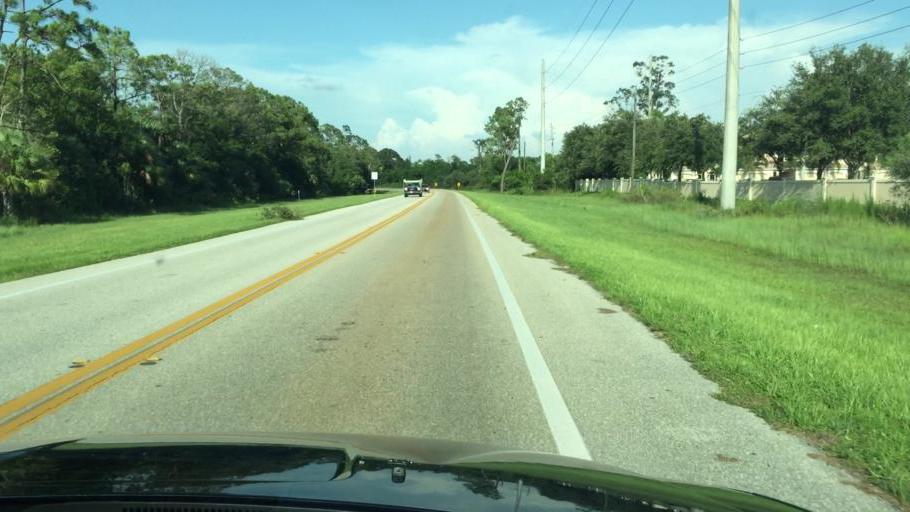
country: US
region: Florida
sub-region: Lee County
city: Gateway
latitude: 26.6273
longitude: -81.7608
